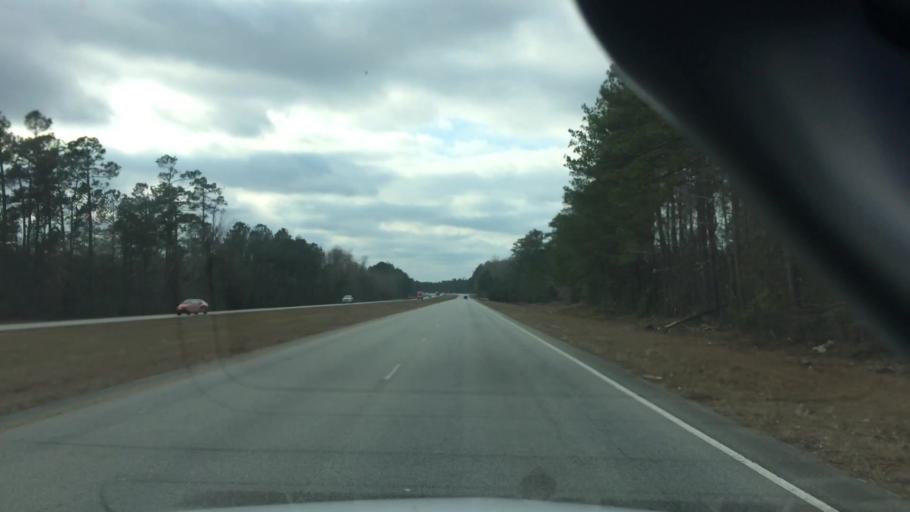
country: US
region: North Carolina
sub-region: Brunswick County
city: Bolivia
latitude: 34.0654
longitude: -78.1890
